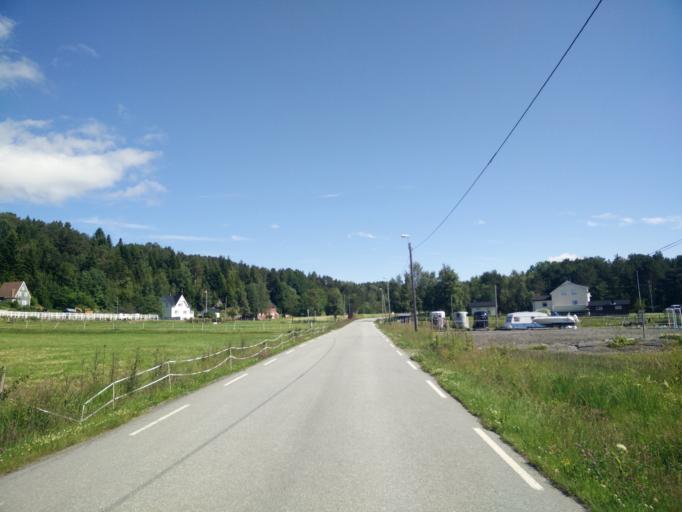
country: NO
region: More og Romsdal
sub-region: Kristiansund
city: Rensvik
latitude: 63.0360
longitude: 7.8246
